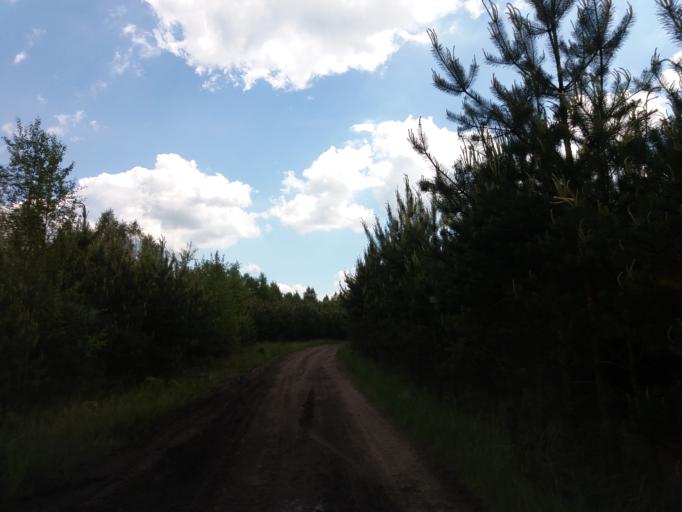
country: PL
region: West Pomeranian Voivodeship
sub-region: Powiat choszczenski
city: Drawno
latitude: 53.2373
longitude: 15.7868
